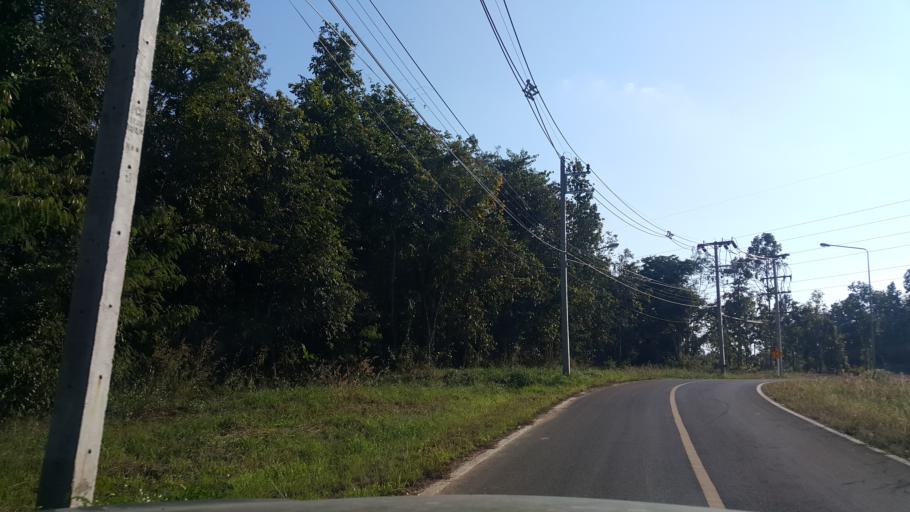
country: TH
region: Lamphun
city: Mae Tha
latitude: 18.5123
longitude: 99.1160
